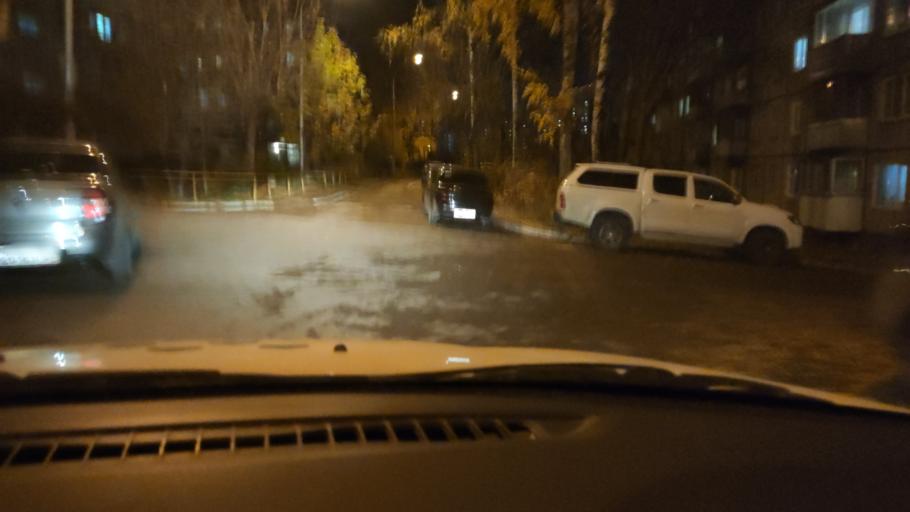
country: RU
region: Perm
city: Perm
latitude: 57.9739
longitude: 56.2292
